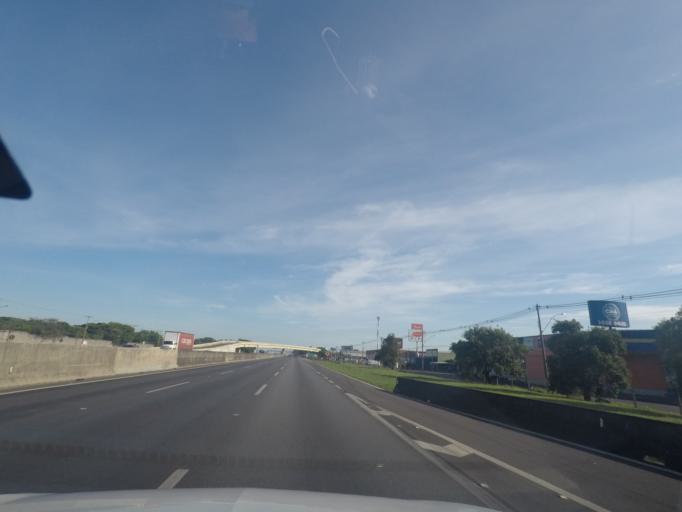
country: BR
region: Sao Paulo
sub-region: Americana
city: Americana
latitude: -22.7191
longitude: -47.2947
